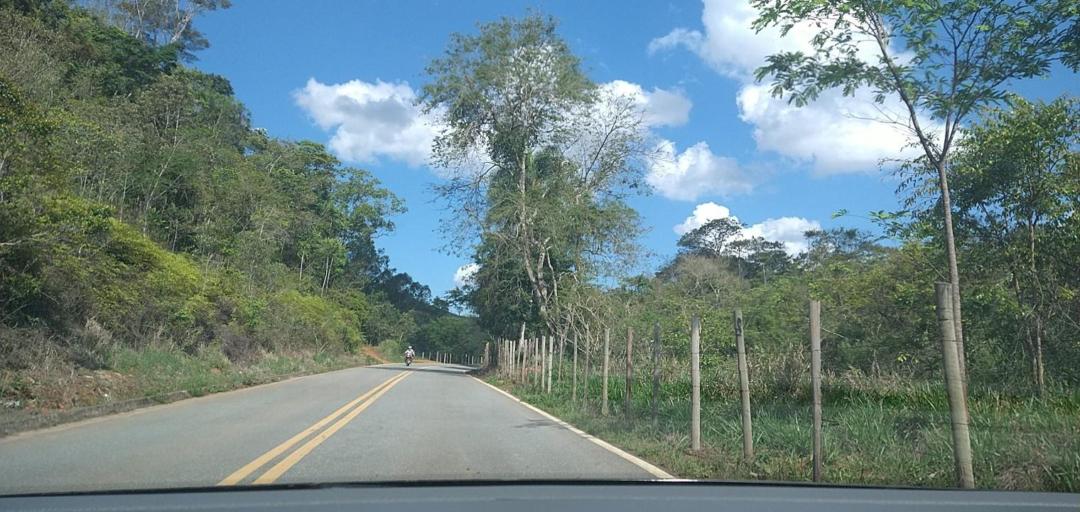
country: BR
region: Minas Gerais
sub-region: Rio Piracicaba
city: Rio Piracicaba
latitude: -19.9967
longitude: -43.1106
